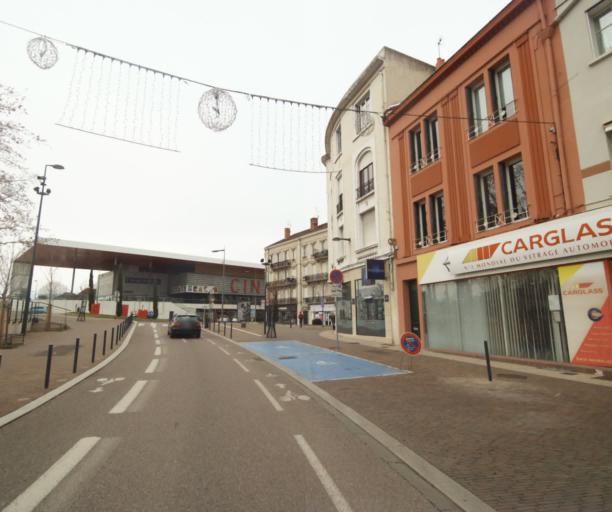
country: FR
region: Rhone-Alpes
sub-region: Departement de la Loire
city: Roanne
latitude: 46.0369
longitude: 4.0660
